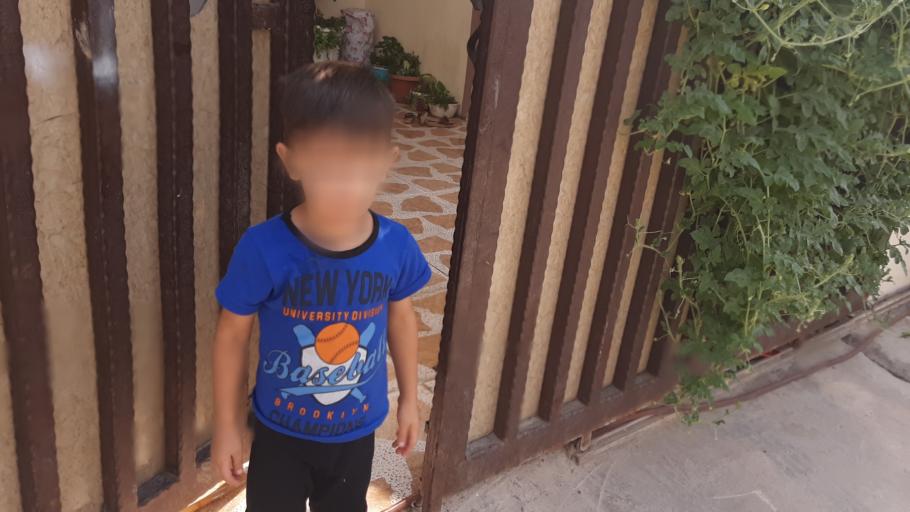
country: IQ
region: Arbil
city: Erbil
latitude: 36.2155
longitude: 44.0969
